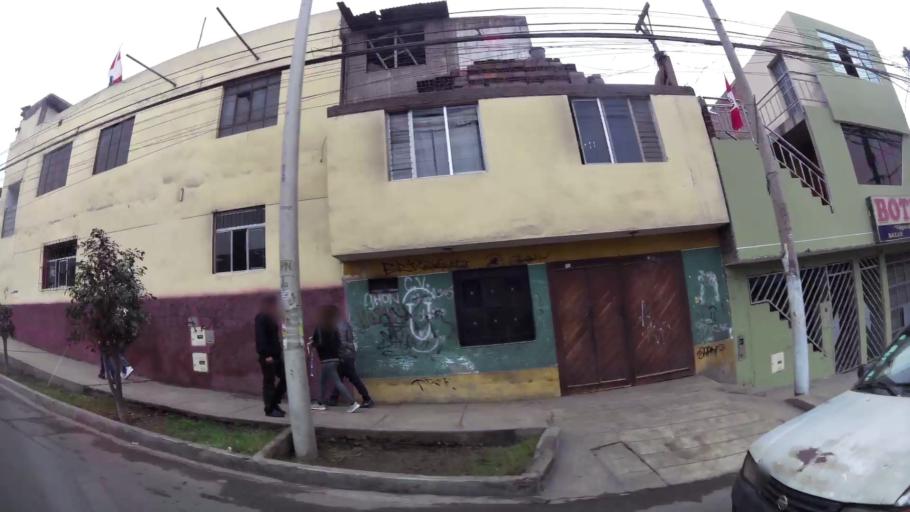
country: PE
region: Lima
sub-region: Lima
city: Surco
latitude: -12.1446
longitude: -76.9687
